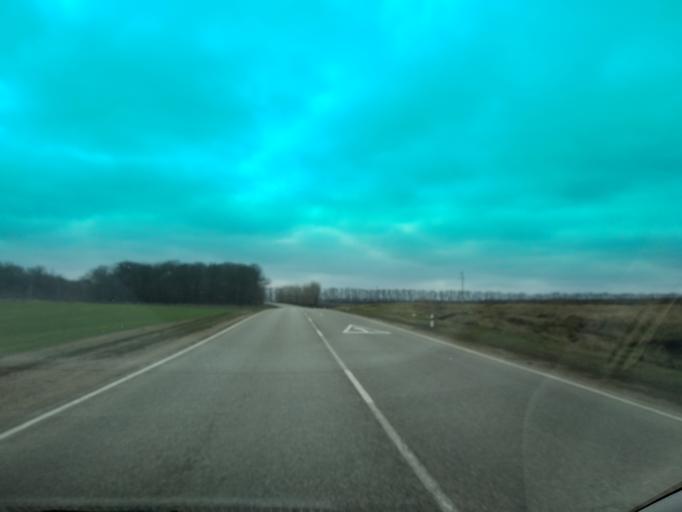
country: RU
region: Krasnodarskiy
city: Novorozhdestvenskaya
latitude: 45.7997
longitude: 39.9829
